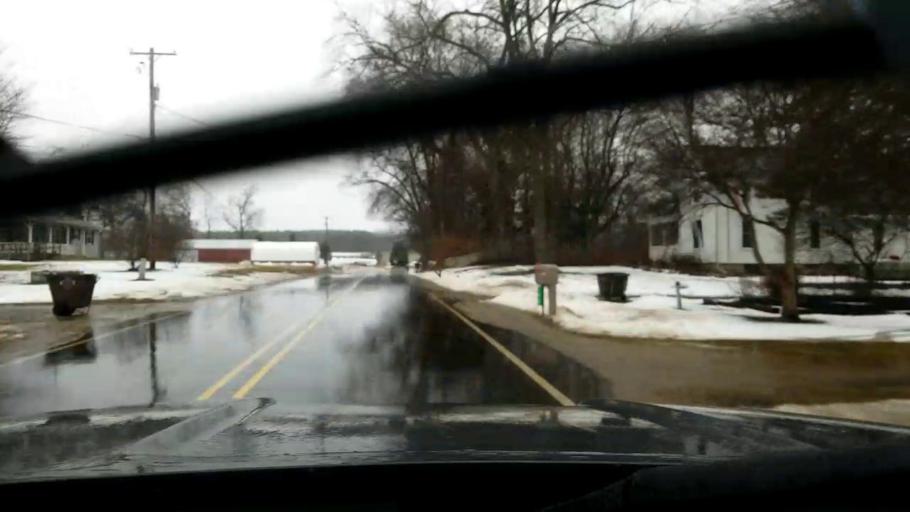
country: US
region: Michigan
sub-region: Jackson County
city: Michigan Center
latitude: 42.3079
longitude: -84.3093
